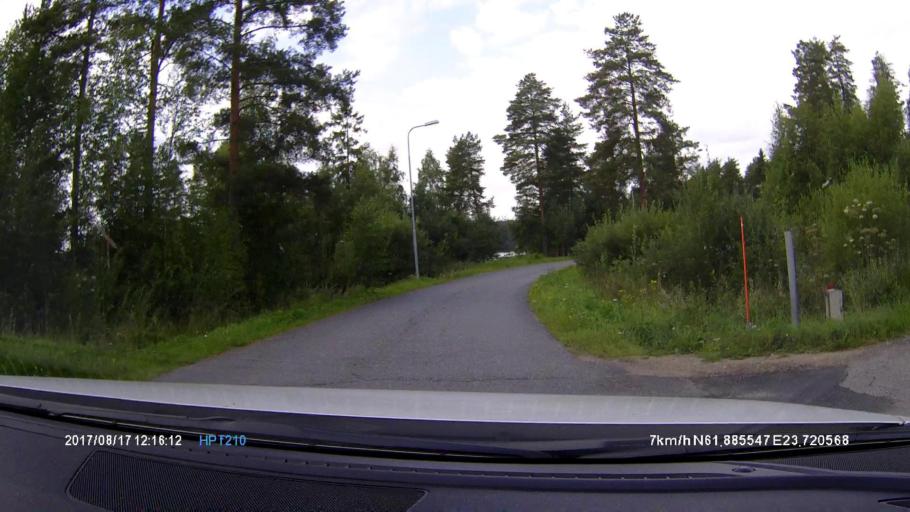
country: FI
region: Pirkanmaa
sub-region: Tampere
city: Kuru
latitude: 61.8857
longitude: 23.7201
